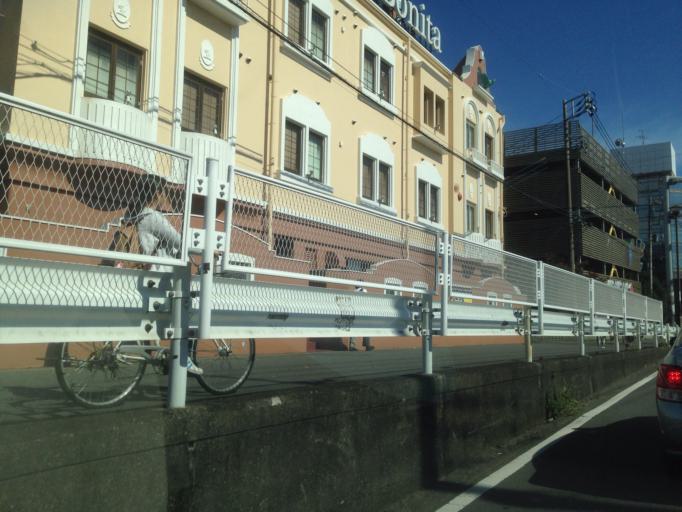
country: JP
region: Tokyo
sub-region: Machida-shi
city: Machida
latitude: 35.5678
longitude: 139.3980
